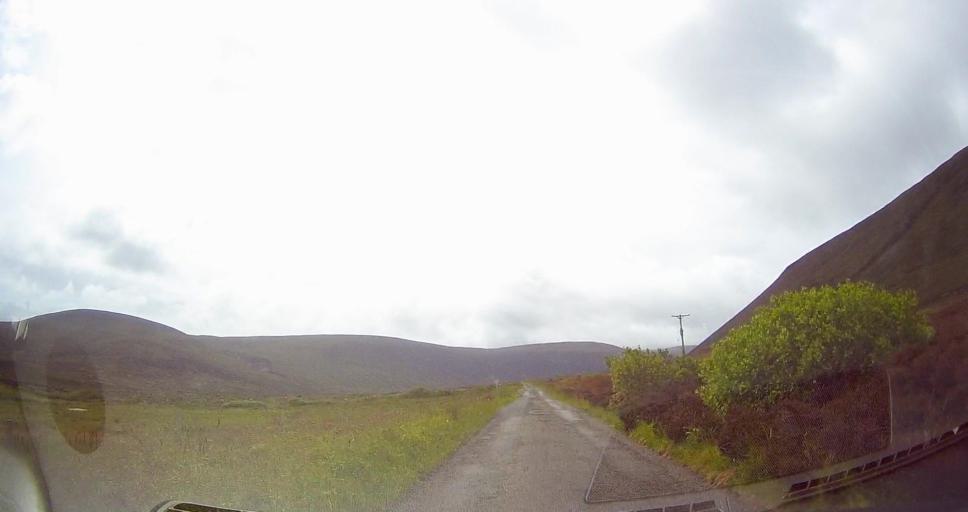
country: GB
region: Scotland
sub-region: Orkney Islands
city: Stromness
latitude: 58.9030
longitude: -3.3165
